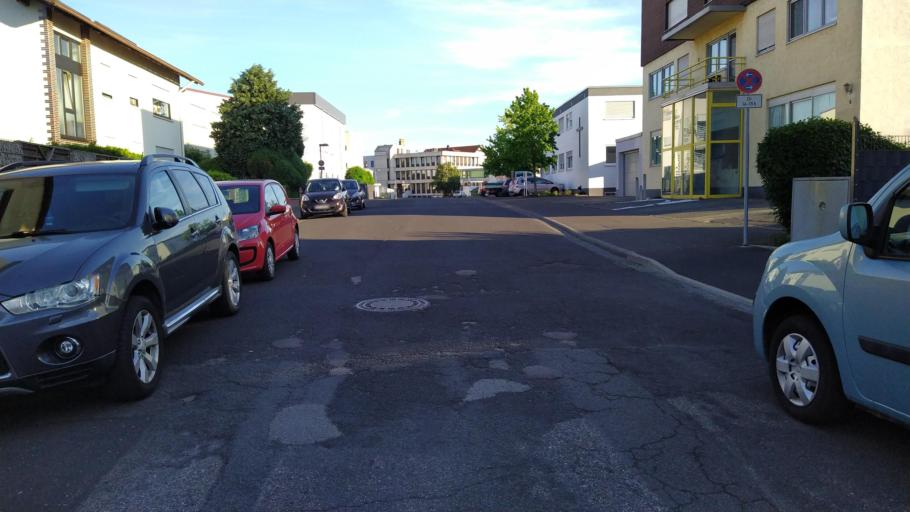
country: DE
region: Bavaria
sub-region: Regierungsbezirk Unterfranken
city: Mainaschaff
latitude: 49.9732
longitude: 9.1106
